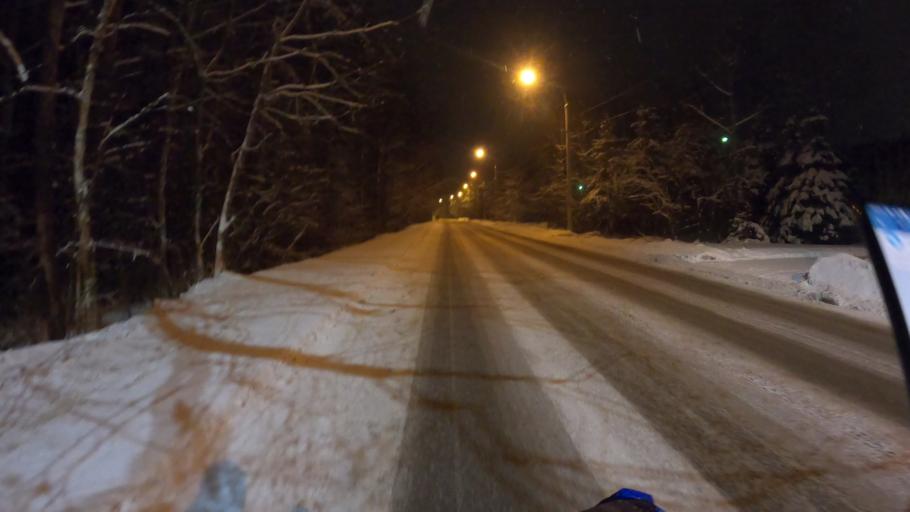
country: RU
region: Moskovskaya
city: Opalikha
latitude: 55.8396
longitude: 37.2208
